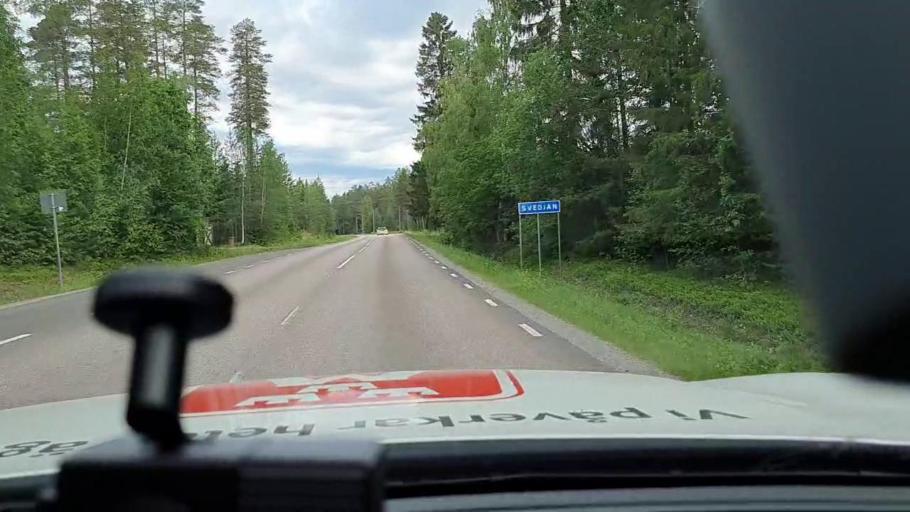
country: SE
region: Norrbotten
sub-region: Bodens Kommun
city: Saevast
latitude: 65.7239
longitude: 21.7512
